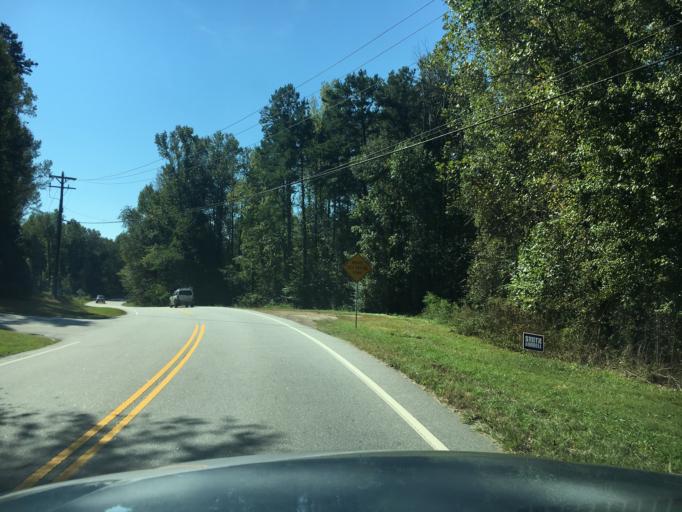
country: US
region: South Carolina
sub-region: Greenville County
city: Taylors
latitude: 34.8833
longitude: -82.2835
